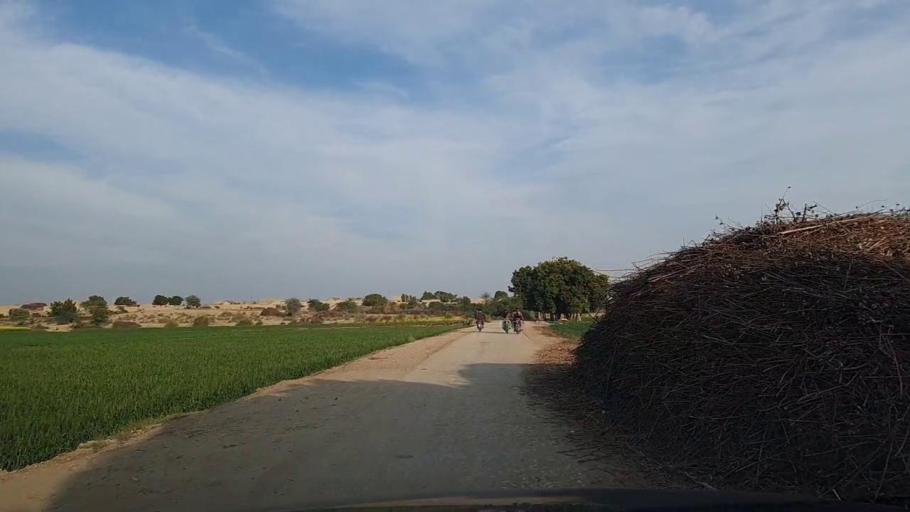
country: PK
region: Sindh
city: Jam Sahib
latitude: 26.4553
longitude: 68.5679
